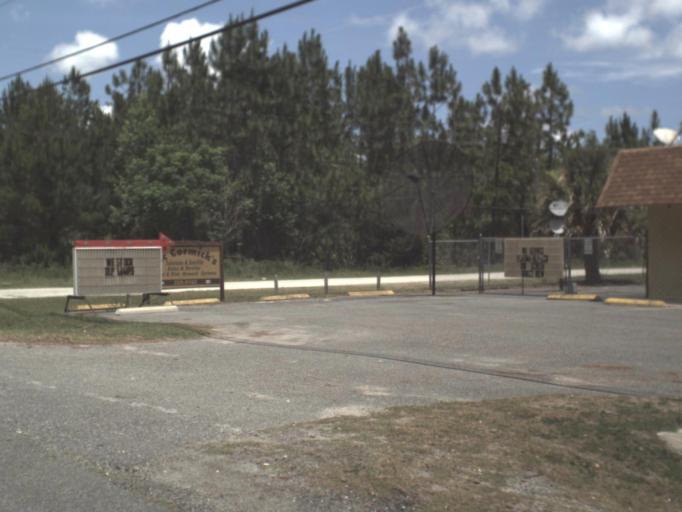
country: US
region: Florida
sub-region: Nassau County
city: Yulee
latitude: 30.6101
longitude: -81.5975
